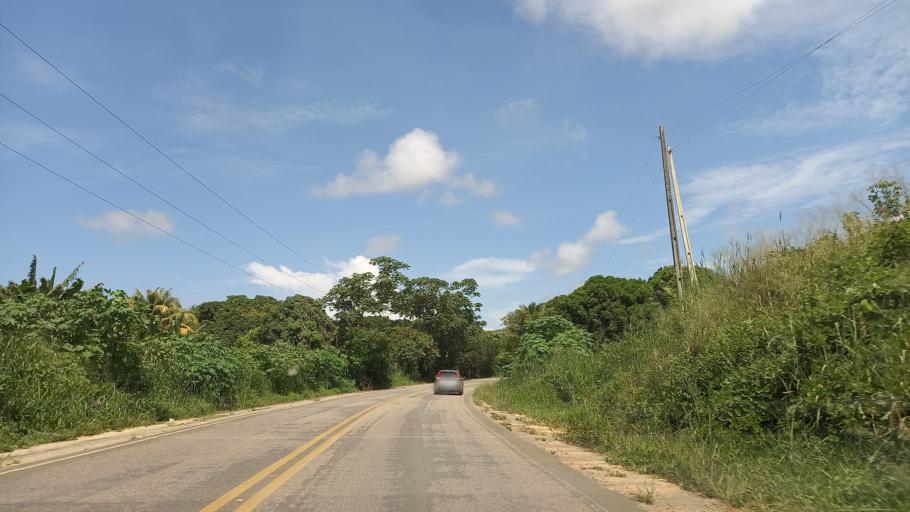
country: BR
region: Pernambuco
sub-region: Barreiros
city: Barreiros
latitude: -8.8253
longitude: -35.1771
